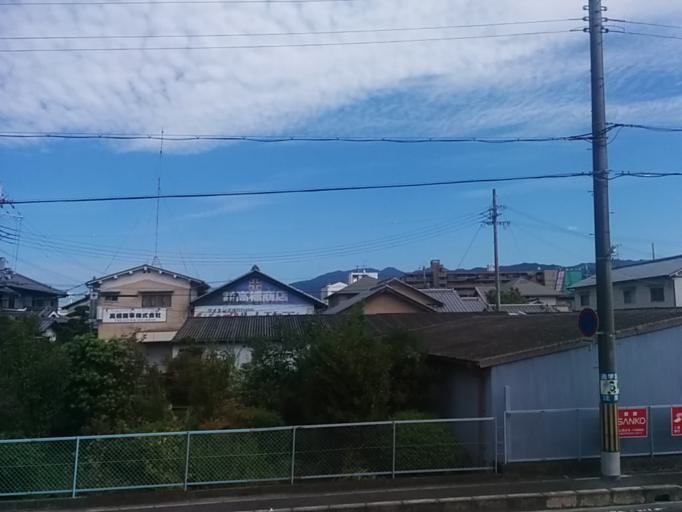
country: JP
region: Nara
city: Kashihara-shi
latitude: 34.4894
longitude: 135.7945
